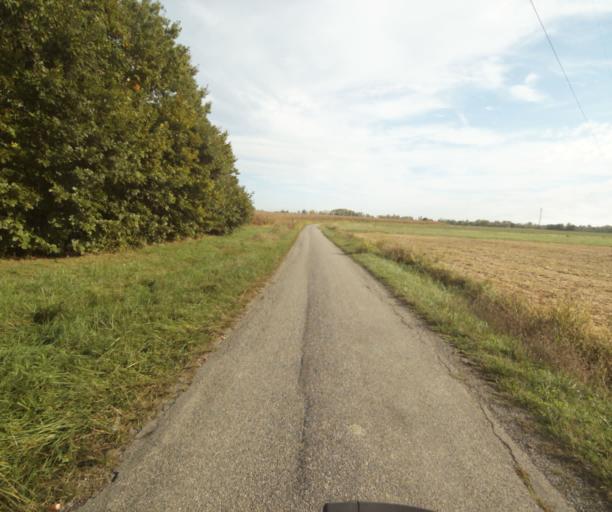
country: FR
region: Midi-Pyrenees
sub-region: Departement du Tarn-et-Garonne
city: Montech
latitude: 43.9793
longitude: 1.2381
